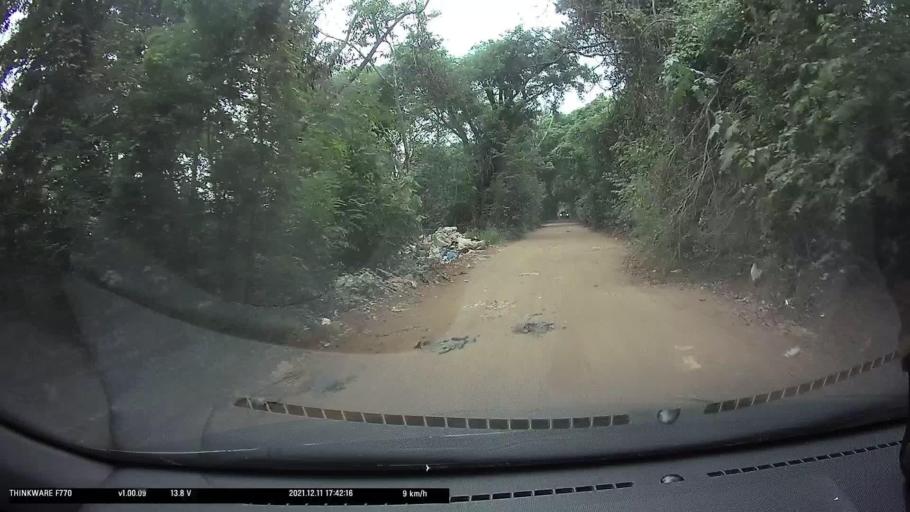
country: PY
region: Cordillera
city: San Bernardino
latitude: -25.2944
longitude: -57.2658
